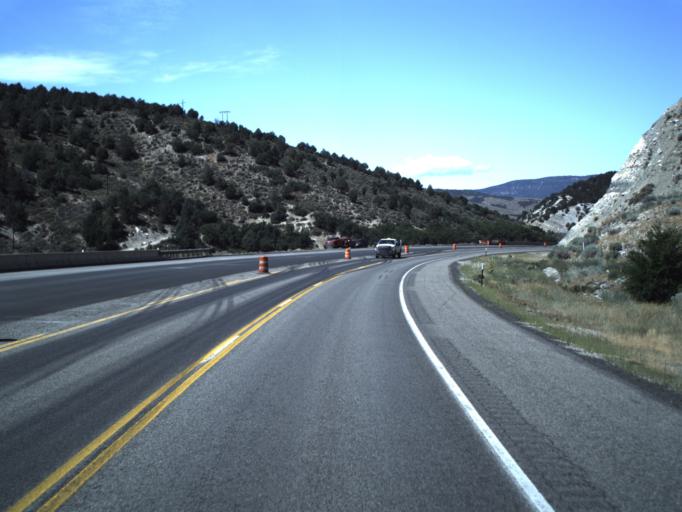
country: US
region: Utah
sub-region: Utah County
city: Mapleton
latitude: 39.9537
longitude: -111.2599
